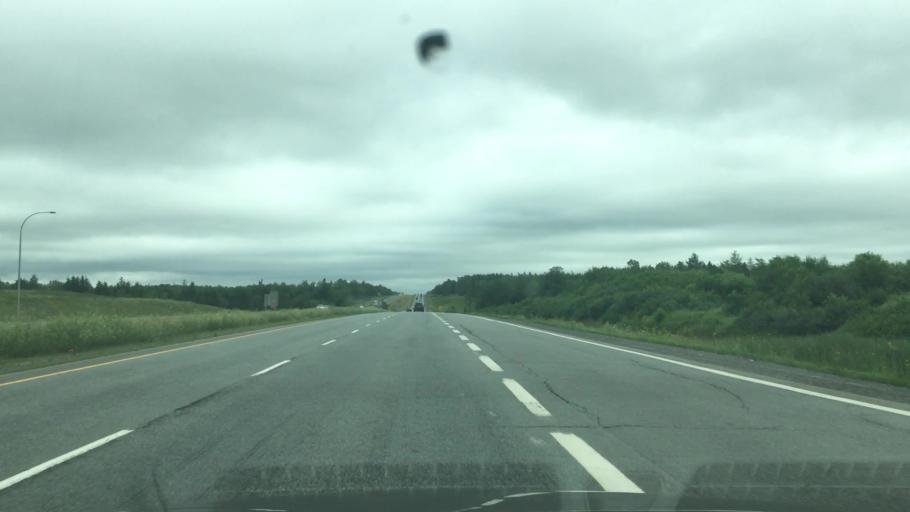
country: CA
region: Nova Scotia
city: Cole Harbour
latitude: 44.9803
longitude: -63.5057
